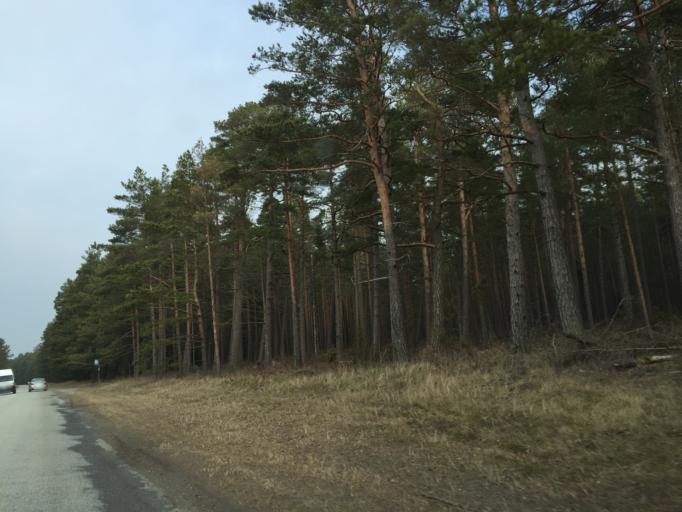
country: LV
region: Salacgrivas
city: Ainazi
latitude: 57.9354
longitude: 24.3917
